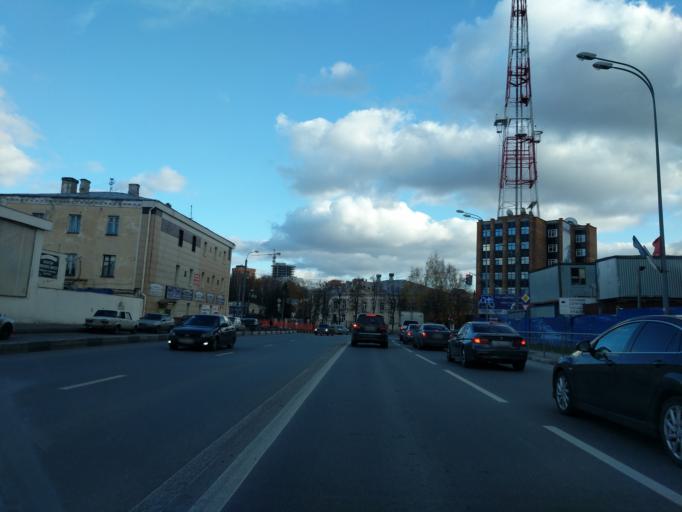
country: RU
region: Nizjnij Novgorod
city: Nizhniy Novgorod
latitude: 56.3091
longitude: 43.9896
